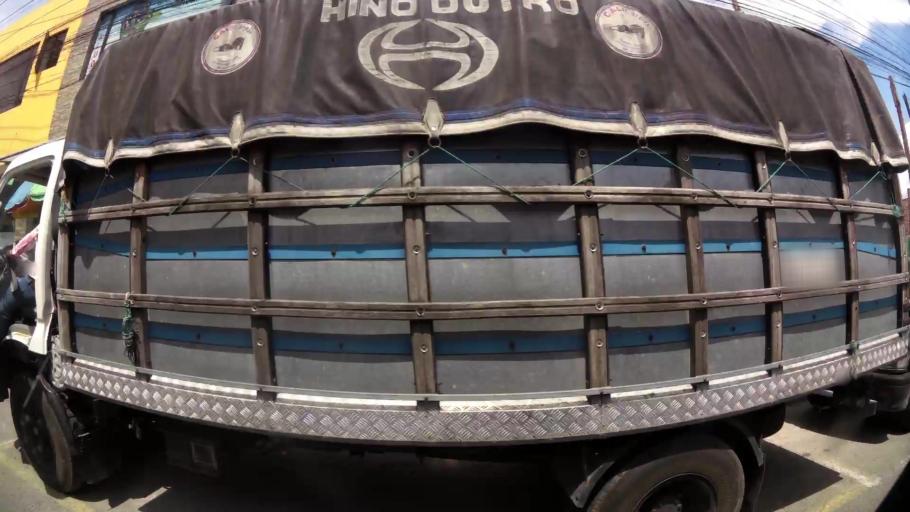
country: EC
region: Pichincha
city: Quito
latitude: -0.2142
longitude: -78.4058
